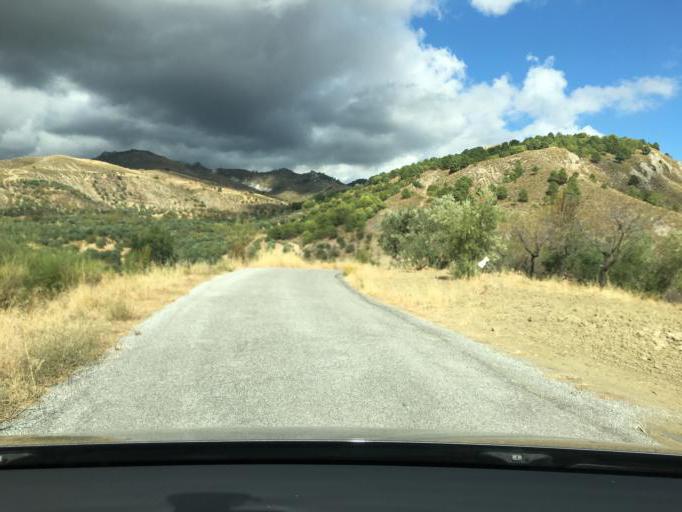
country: ES
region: Andalusia
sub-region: Provincia de Granada
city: Quentar
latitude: 37.2076
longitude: -3.4662
